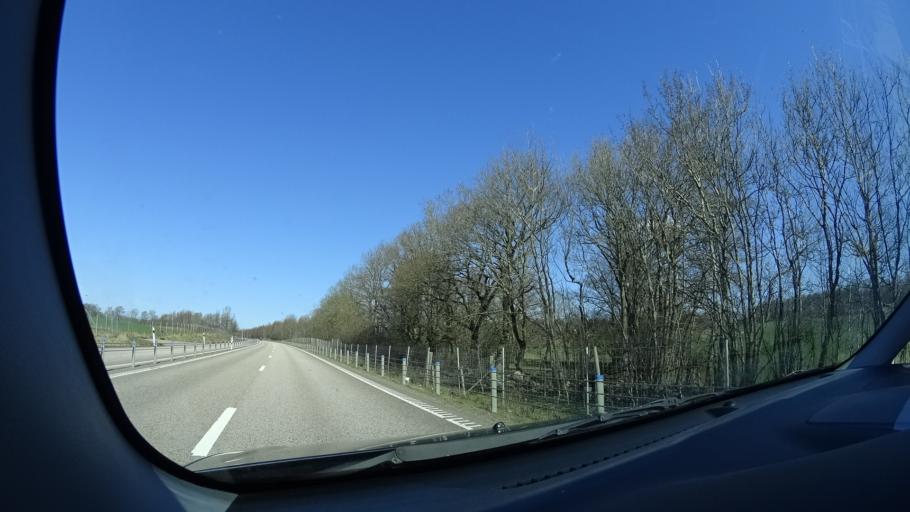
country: SE
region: Skane
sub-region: Astorps Kommun
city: Astorp
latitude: 56.1765
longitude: 12.9073
